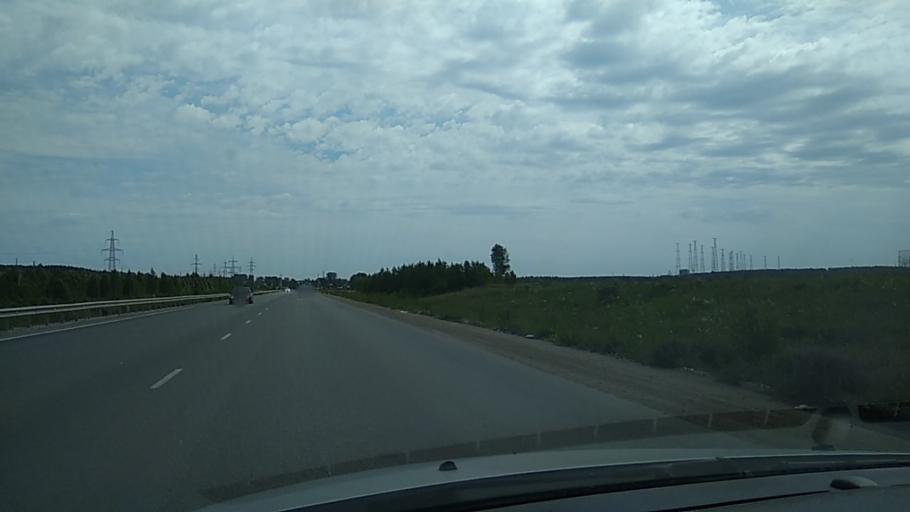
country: RU
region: Sverdlovsk
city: Verkhnyaya Pyshma
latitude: 56.9518
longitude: 60.5875
